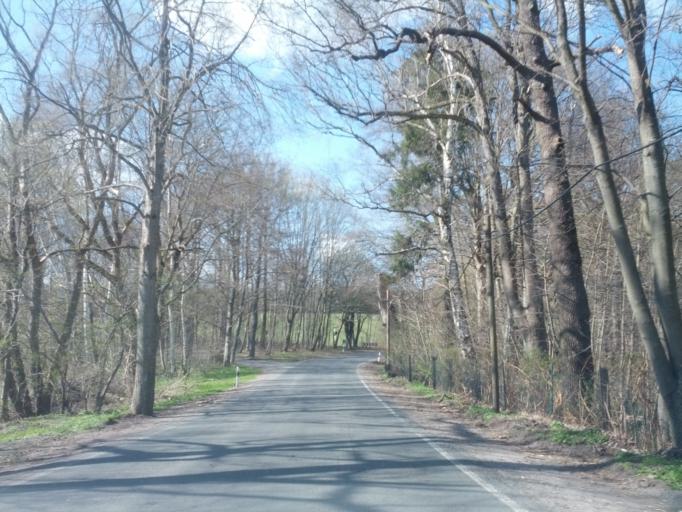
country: DE
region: Thuringia
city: Friedrichroda
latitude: 50.8655
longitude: 10.5549
